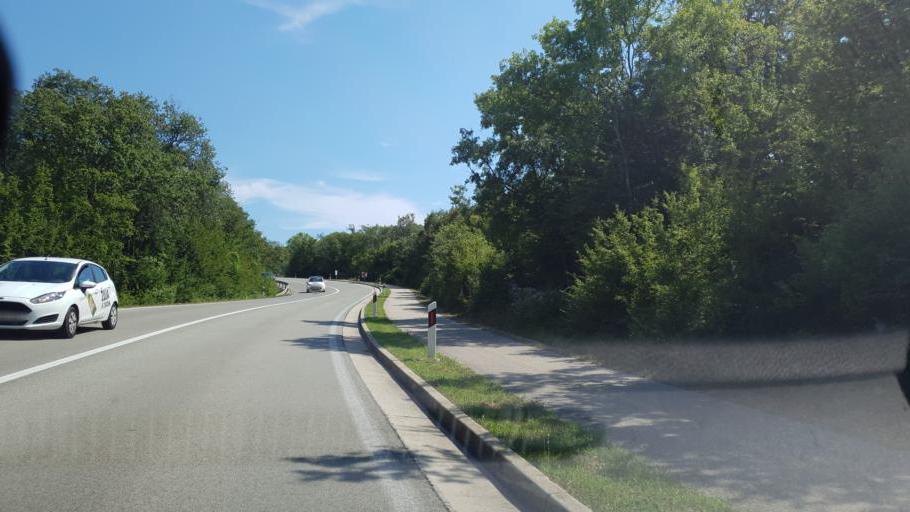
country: HR
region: Primorsko-Goranska
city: Njivice
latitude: 45.0899
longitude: 14.5397
